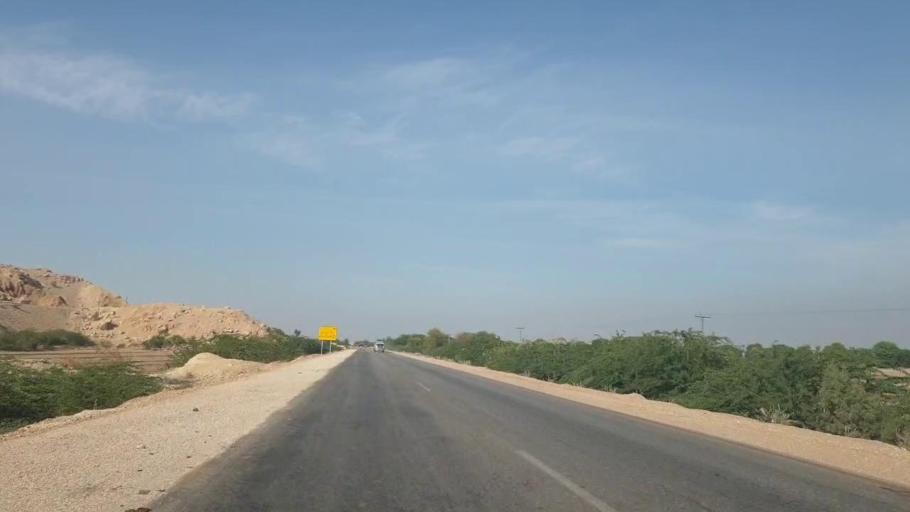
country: PK
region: Sindh
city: Sehwan
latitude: 26.3079
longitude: 67.8928
